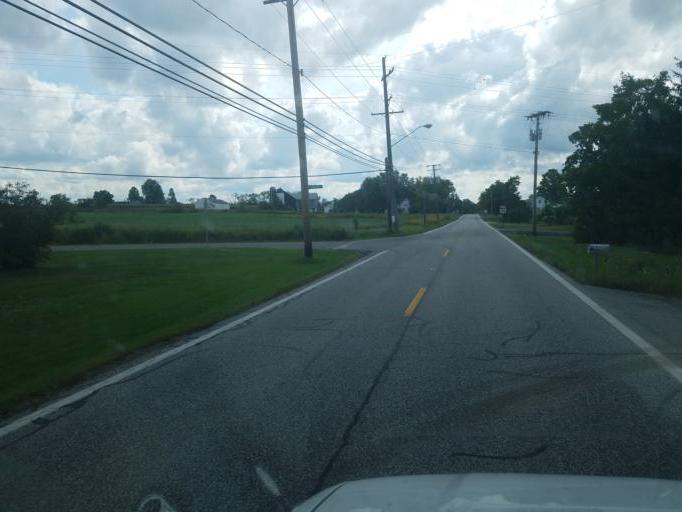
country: US
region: Ohio
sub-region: Geauga County
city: Burton
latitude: 41.4339
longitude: -81.1418
